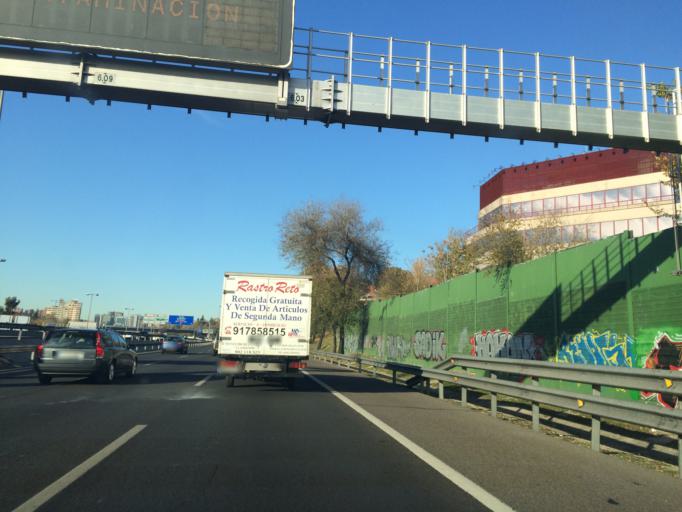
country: ES
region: Madrid
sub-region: Provincia de Madrid
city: Ciudad Lineal
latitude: 40.4546
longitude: -3.6629
